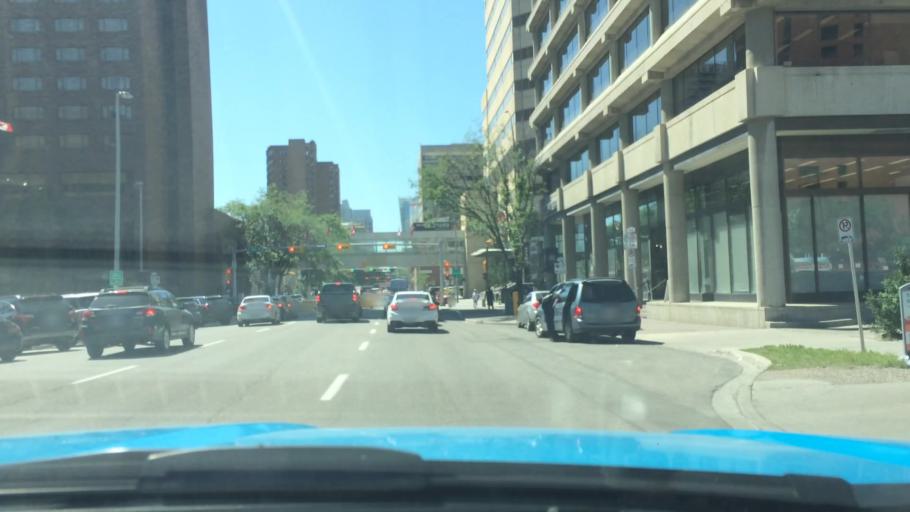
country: CA
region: Alberta
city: Calgary
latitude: 51.0499
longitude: -114.0603
